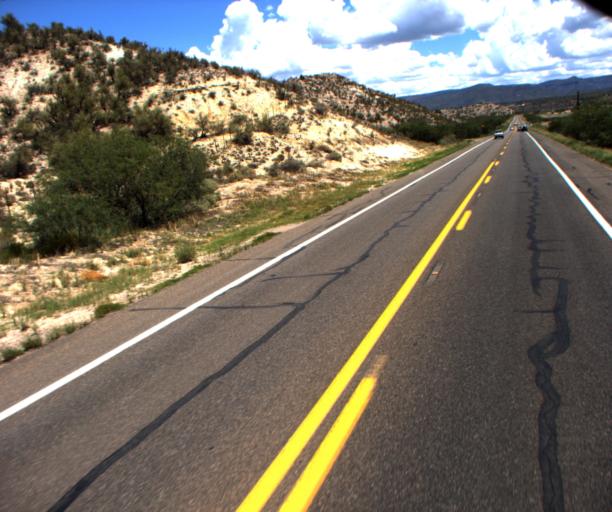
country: US
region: Arizona
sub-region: Yavapai County
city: Camp Verde
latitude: 34.5279
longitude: -111.7987
